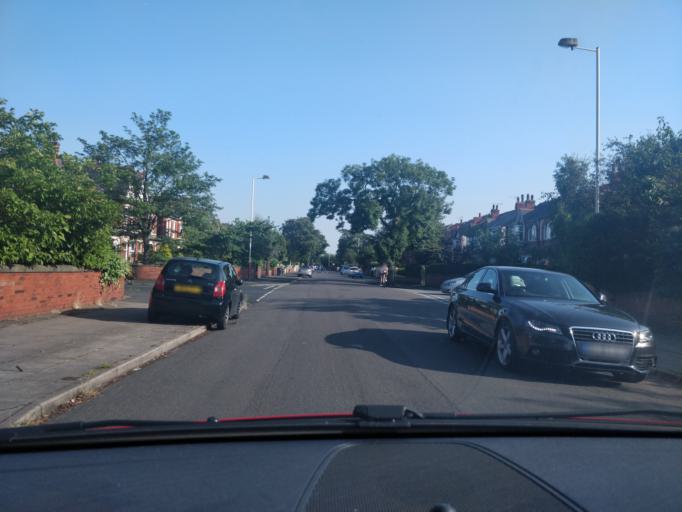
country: GB
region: England
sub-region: Sefton
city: Southport
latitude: 53.6522
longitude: -2.9744
